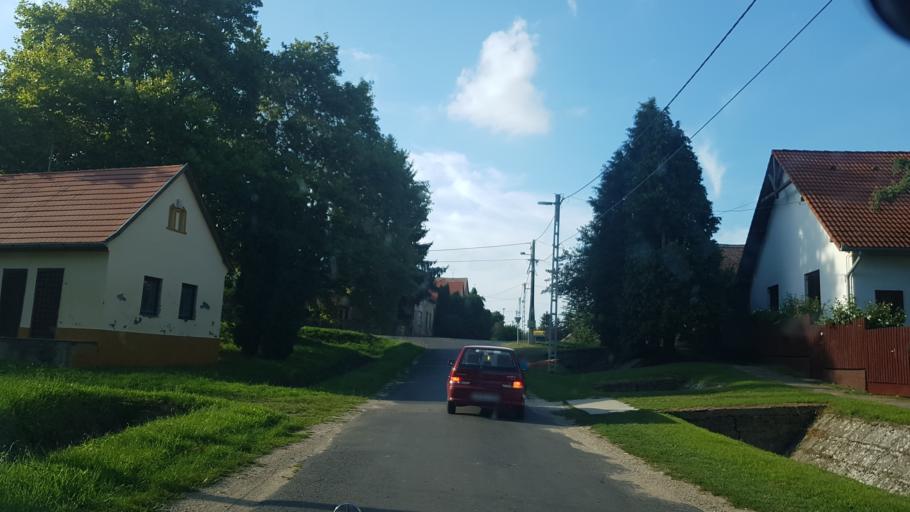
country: HU
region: Somogy
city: Segesd
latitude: 46.3311
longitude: 17.3416
